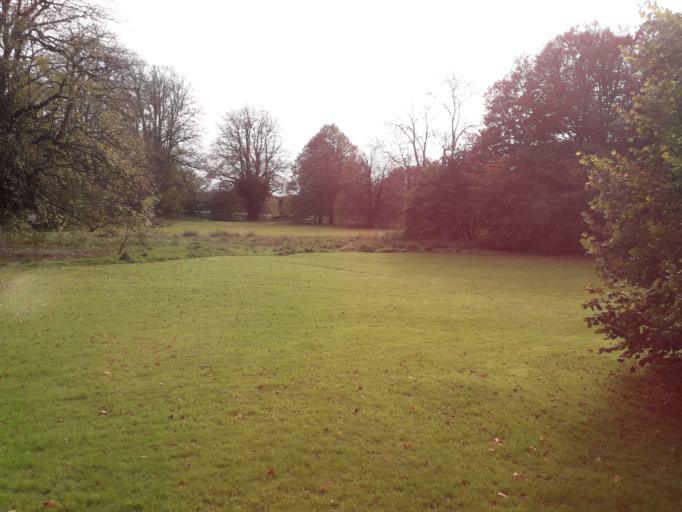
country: IE
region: Leinster
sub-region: Laois
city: Mountrath
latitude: 53.0276
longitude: -7.5247
